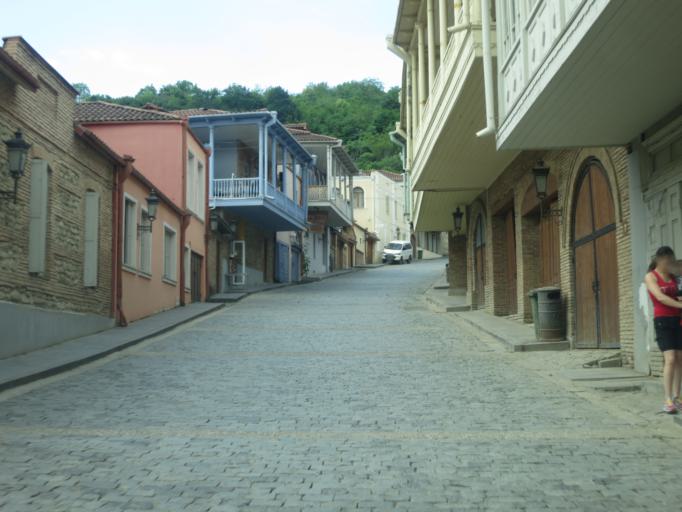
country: GE
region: Kakheti
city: Sighnaghi
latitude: 41.6165
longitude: 45.9205
